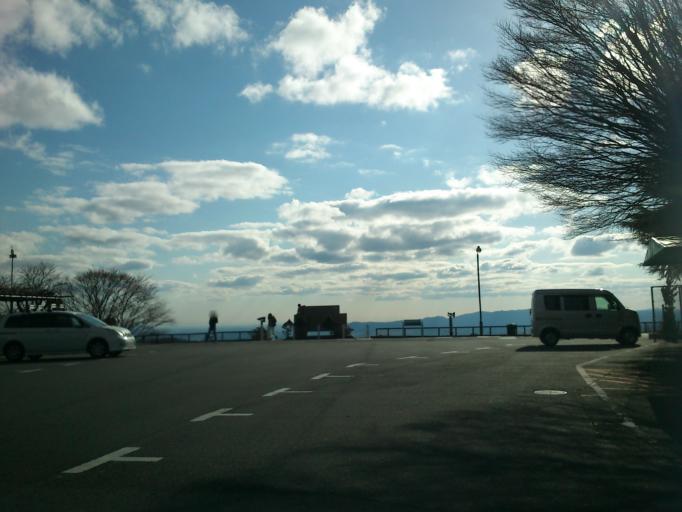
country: JP
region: Shiga Prefecture
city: Otsu-shi
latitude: 35.0530
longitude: 135.8317
